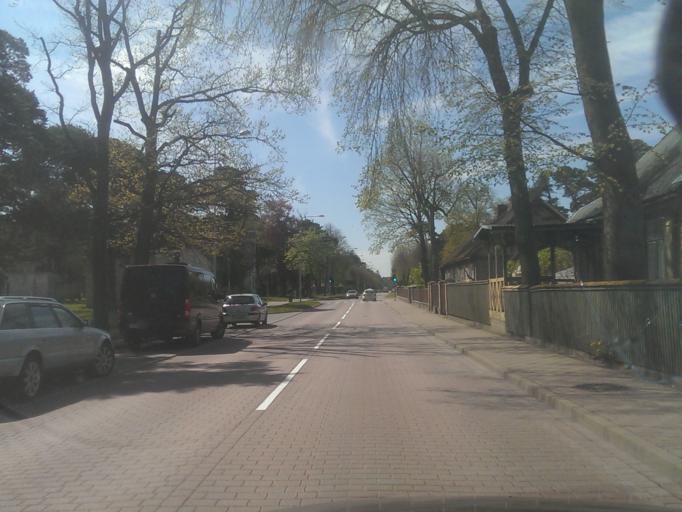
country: LV
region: Ventspils
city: Ventspils
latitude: 57.3911
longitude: 21.5482
